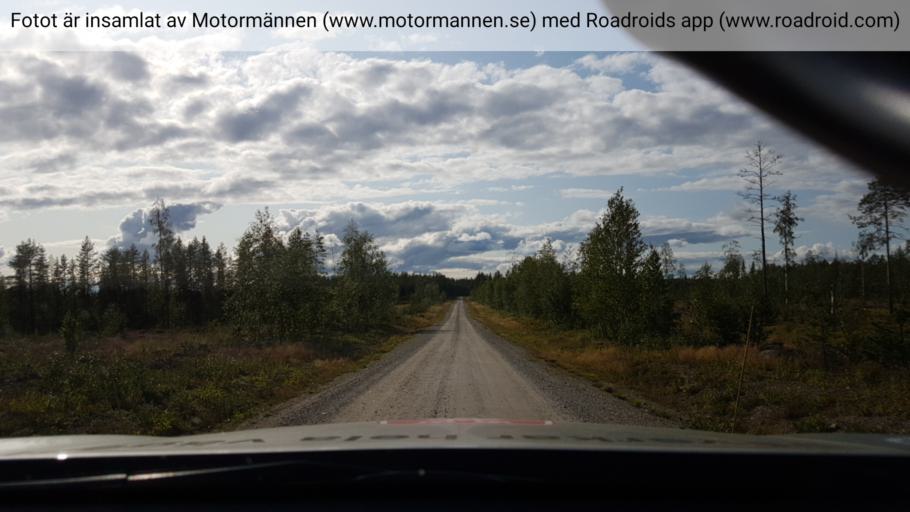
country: SE
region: Vaesterbotten
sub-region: Lycksele Kommun
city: Lycksele
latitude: 64.7163
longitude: 18.9708
